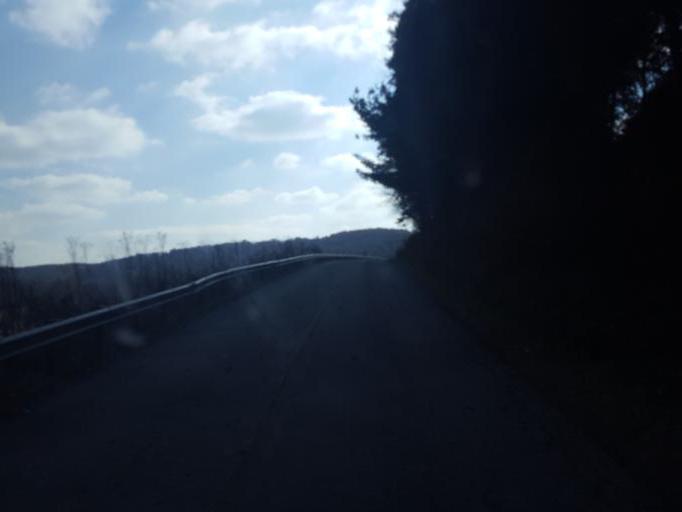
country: US
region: Ohio
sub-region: Ashland County
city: Loudonville
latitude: 40.5901
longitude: -82.1678
